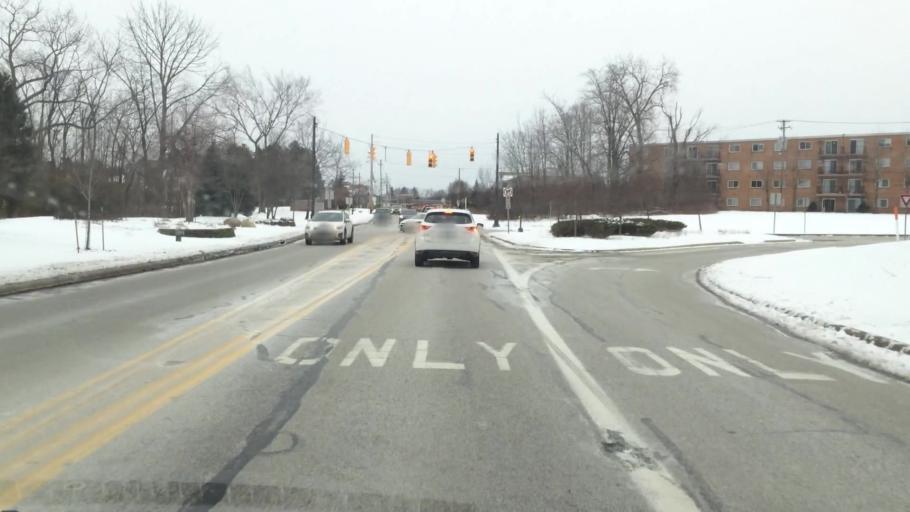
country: US
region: Ohio
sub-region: Cuyahoga County
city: Orange
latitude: 41.4648
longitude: -81.4838
